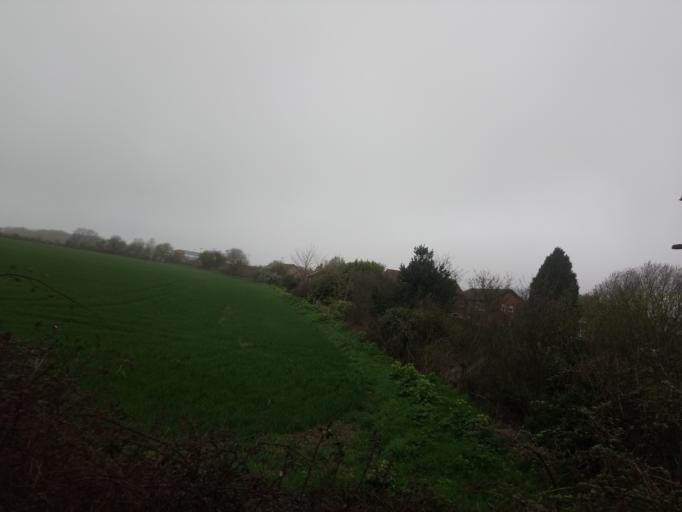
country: GB
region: England
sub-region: Suffolk
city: Saxmundham
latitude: 52.2123
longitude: 1.4880
